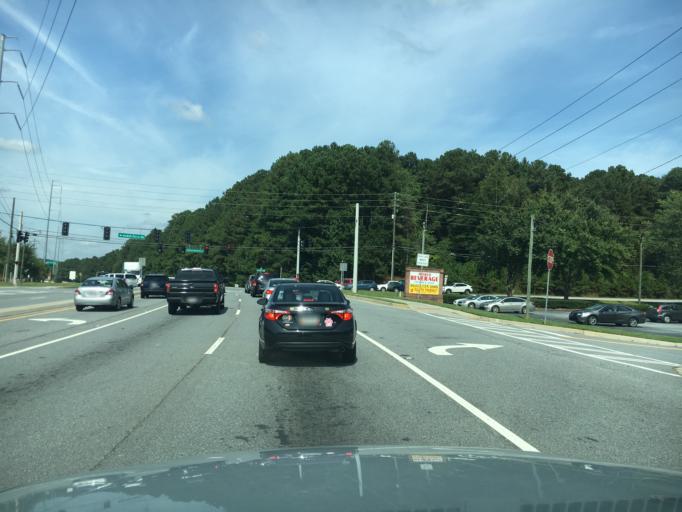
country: US
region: Georgia
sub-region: Gwinnett County
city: Duluth
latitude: 34.0016
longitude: -84.1623
